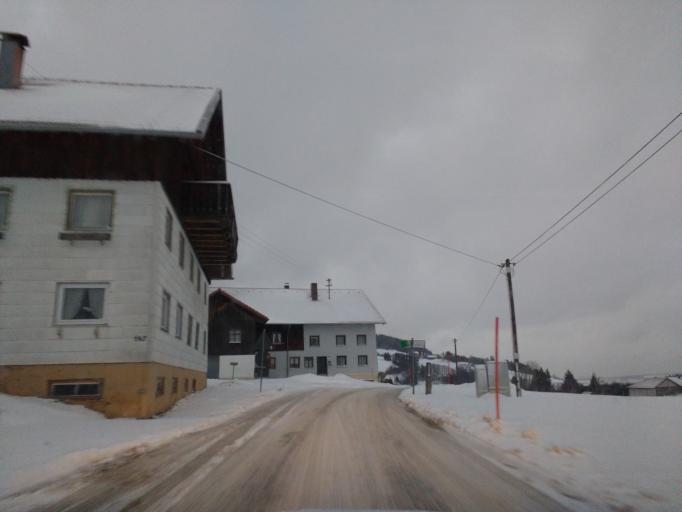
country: DE
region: Bavaria
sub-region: Swabia
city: Buchenberg
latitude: 47.7132
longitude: 10.2162
